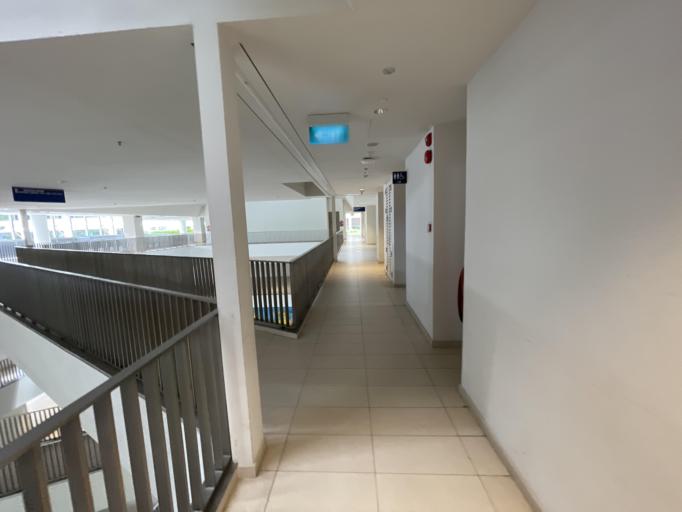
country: SG
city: Singapore
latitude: 1.2958
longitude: 103.7721
